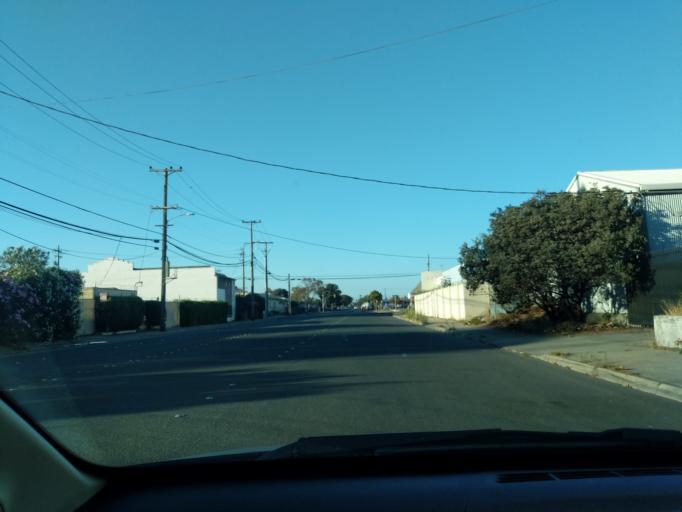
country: US
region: California
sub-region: Contra Costa County
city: Richmond
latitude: 37.9230
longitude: -122.3558
